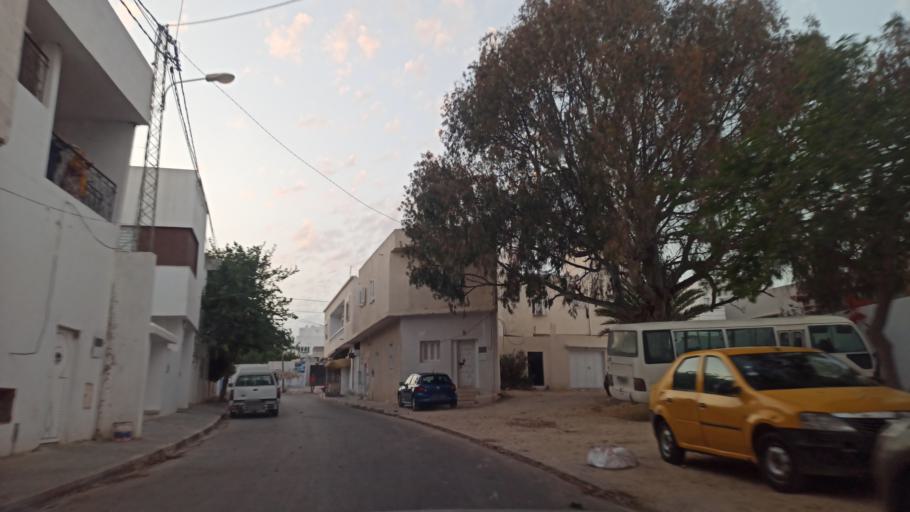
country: TN
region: Nabul
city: Al Hammamat
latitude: 36.4051
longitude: 10.6205
